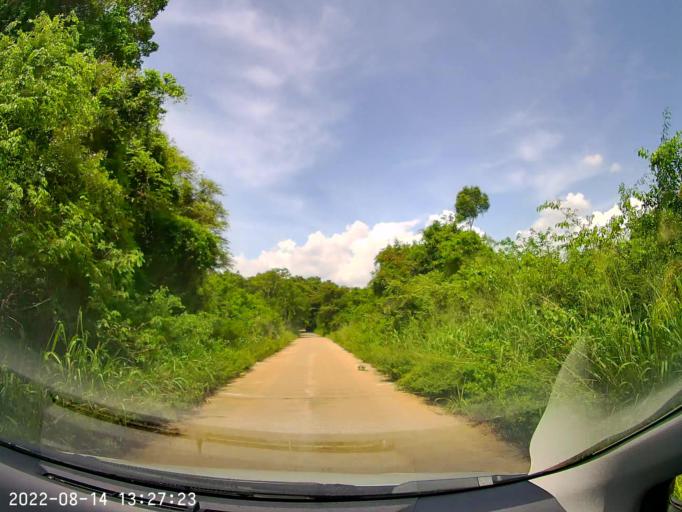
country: LK
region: Central
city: Sigiriya
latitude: 7.9710
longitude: 80.7651
